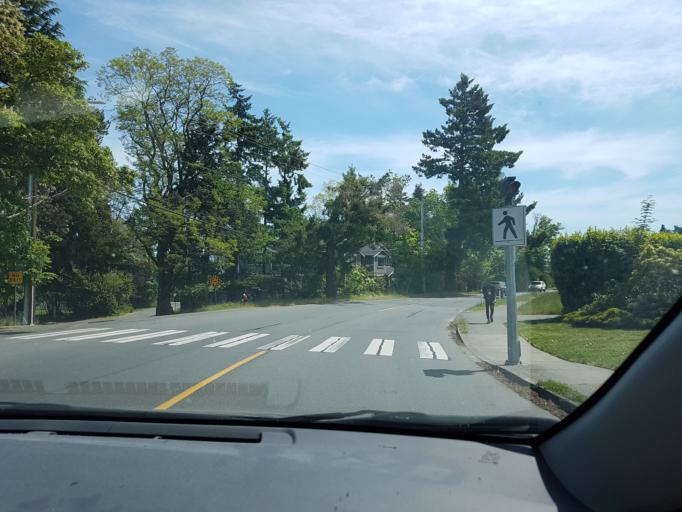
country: CA
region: British Columbia
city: Oak Bay
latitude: 48.4849
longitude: -123.3067
